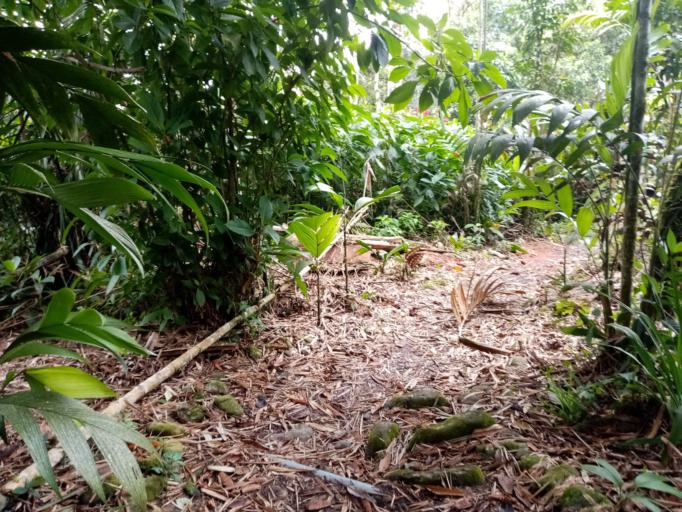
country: EC
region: Napo
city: Tena
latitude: -0.9722
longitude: -77.8007
